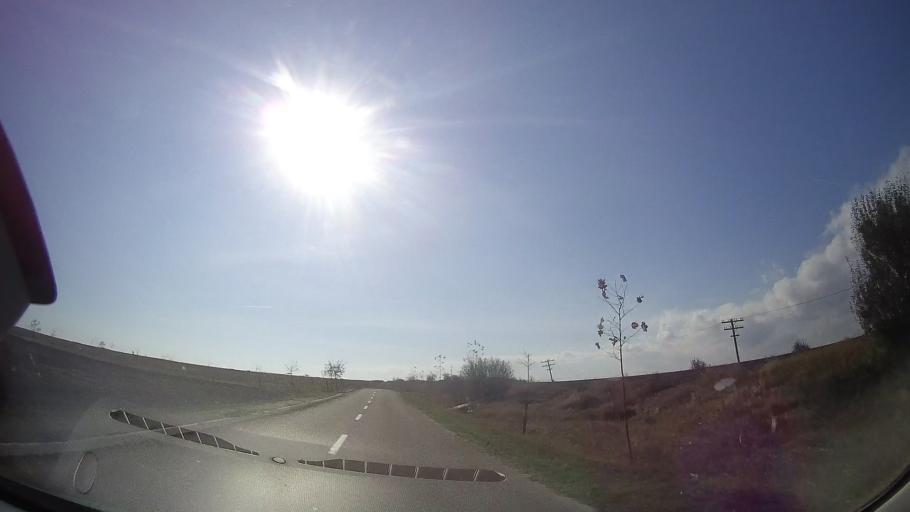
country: RO
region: Constanta
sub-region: Comuna Costinesti
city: Schitu
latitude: 43.9229
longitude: 28.6317
